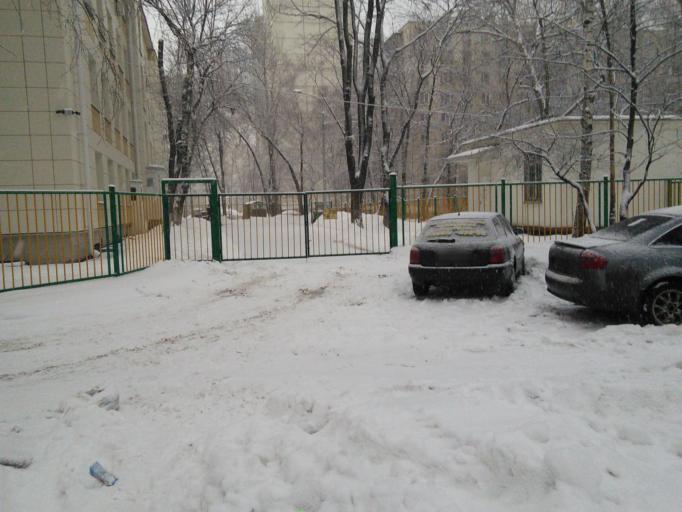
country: RU
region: Moscow
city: Kozeyevo
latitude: 55.8815
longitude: 37.6402
